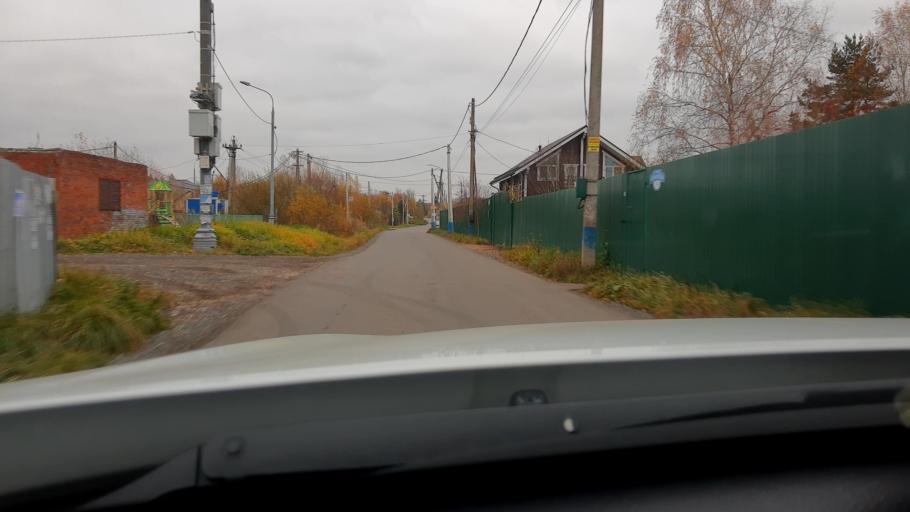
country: RU
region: Moscow
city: Tolstopal'tsevo
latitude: 55.6051
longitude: 37.2348
